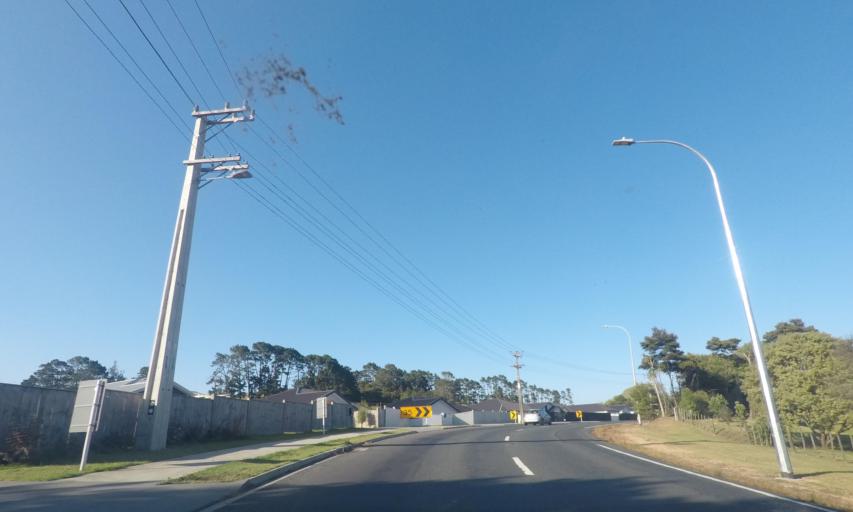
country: NZ
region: Auckland
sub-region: Auckland
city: Muriwai Beach
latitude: -36.7751
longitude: 174.4891
